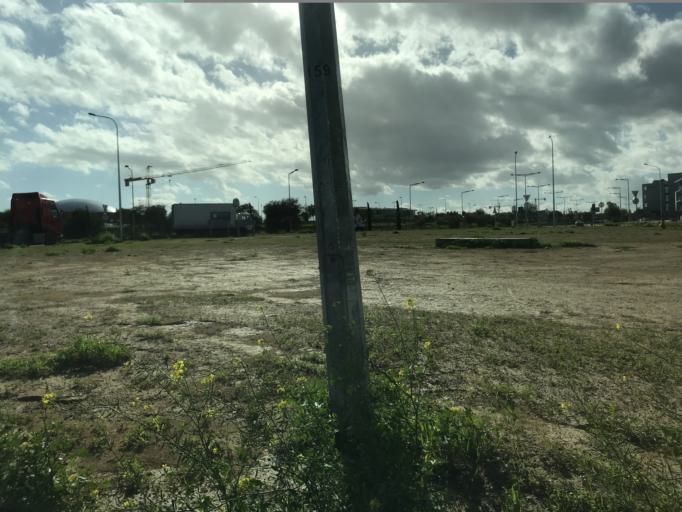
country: CY
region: Lefkosia
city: Geri
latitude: 35.1498
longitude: 33.4108
